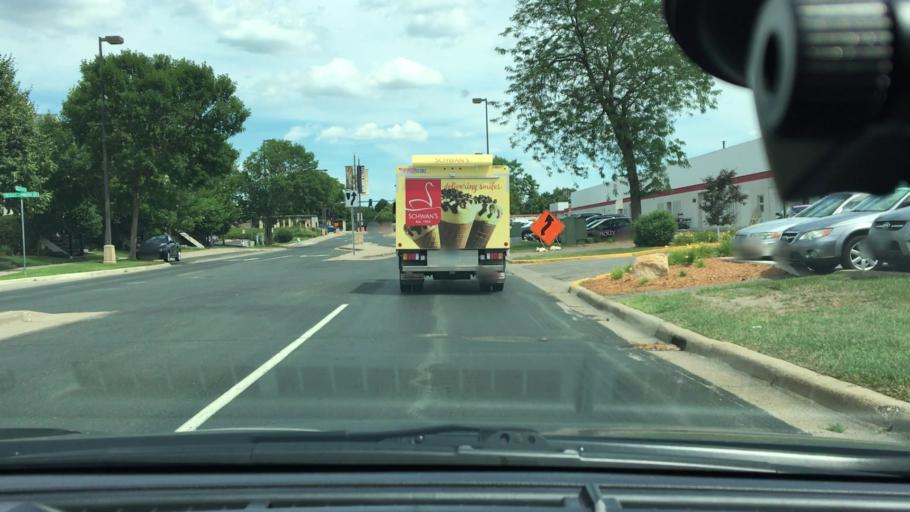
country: US
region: Minnesota
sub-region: Hennepin County
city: Golden Valley
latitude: 44.9855
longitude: -93.3827
